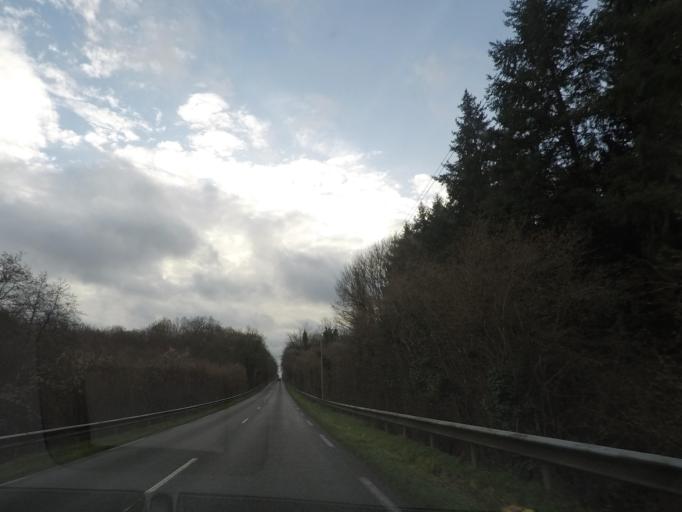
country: FR
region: Pays de la Loire
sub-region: Departement de la Sarthe
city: Cherre
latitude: 48.1415
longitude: 0.6912
